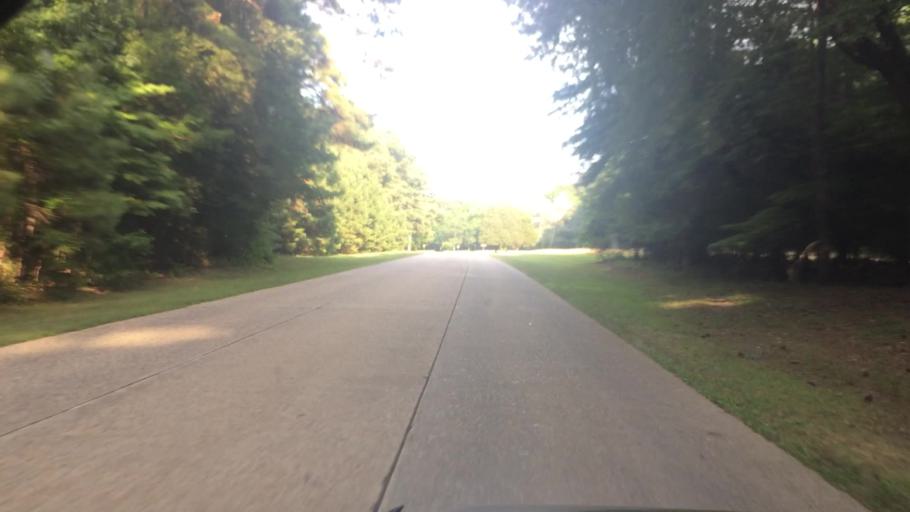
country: US
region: Virginia
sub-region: James City County
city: Williamsburg
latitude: 37.2185
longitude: -76.7619
